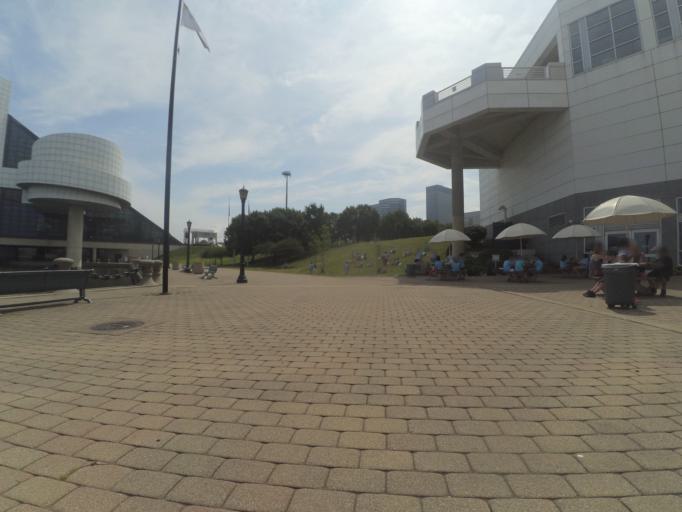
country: US
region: Ohio
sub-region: Cuyahoga County
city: Cleveland
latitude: 41.5077
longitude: -81.6965
